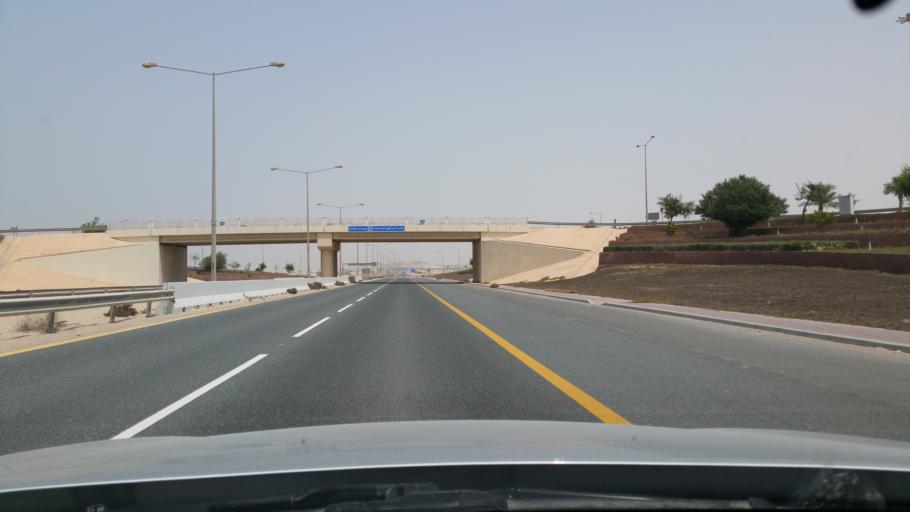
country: QA
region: Baladiyat ar Rayyan
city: Dukhan
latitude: 25.3869
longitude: 50.7824
